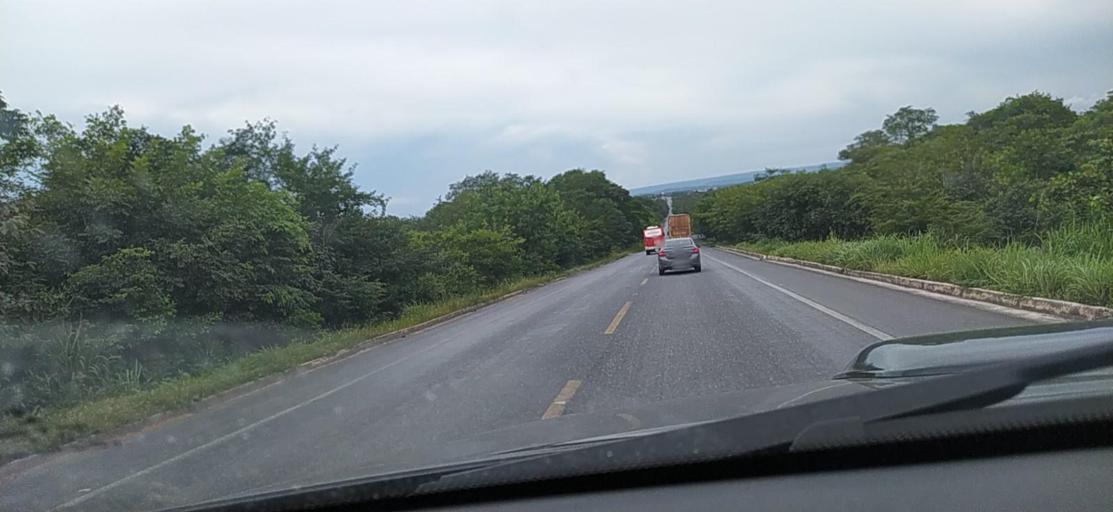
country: BR
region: Minas Gerais
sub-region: Montes Claros
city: Montes Claros
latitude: -16.6617
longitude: -43.7612
